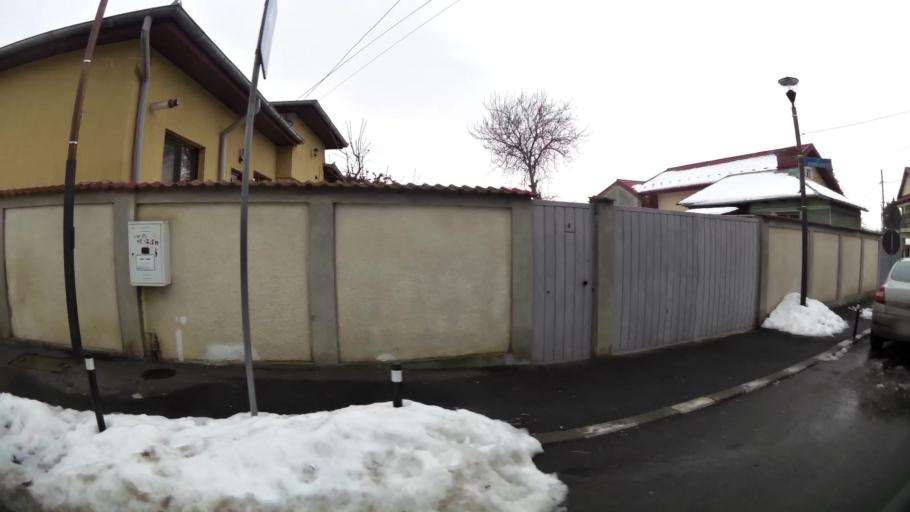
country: RO
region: Ilfov
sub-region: Comuna Pantelimon
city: Pantelimon
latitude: 44.4497
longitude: 26.2073
